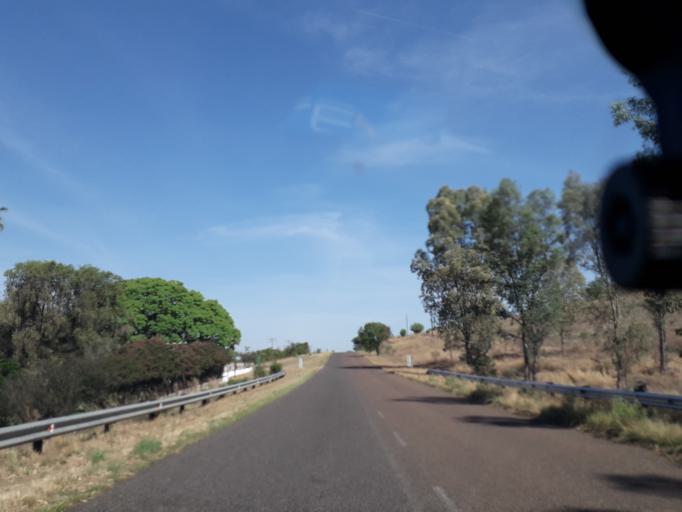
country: ZA
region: Limpopo
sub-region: Waterberg District Municipality
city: Warmbaths
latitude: -24.8341
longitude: 28.2297
